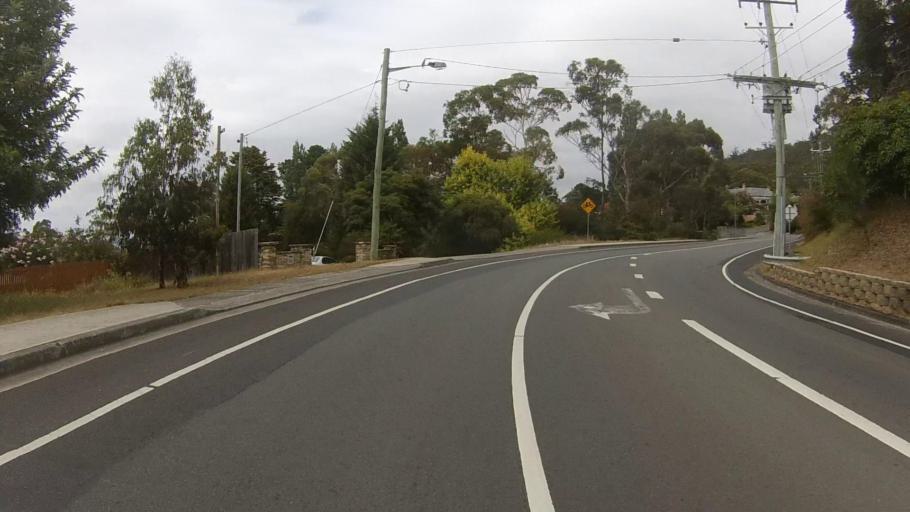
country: AU
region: Tasmania
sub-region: Kingborough
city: Taroona
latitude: -42.9338
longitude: 147.3556
